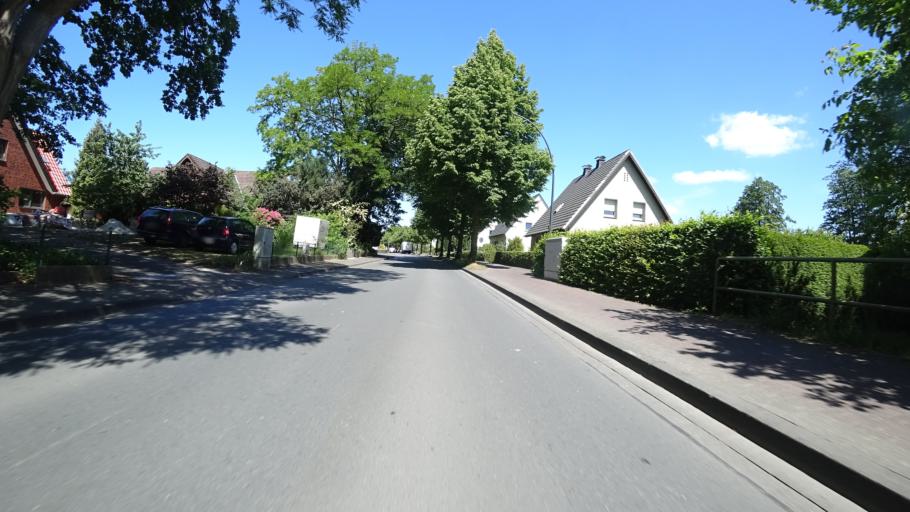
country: DE
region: North Rhine-Westphalia
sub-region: Regierungsbezirk Detmold
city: Guetersloh
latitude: 51.9205
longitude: 8.4289
